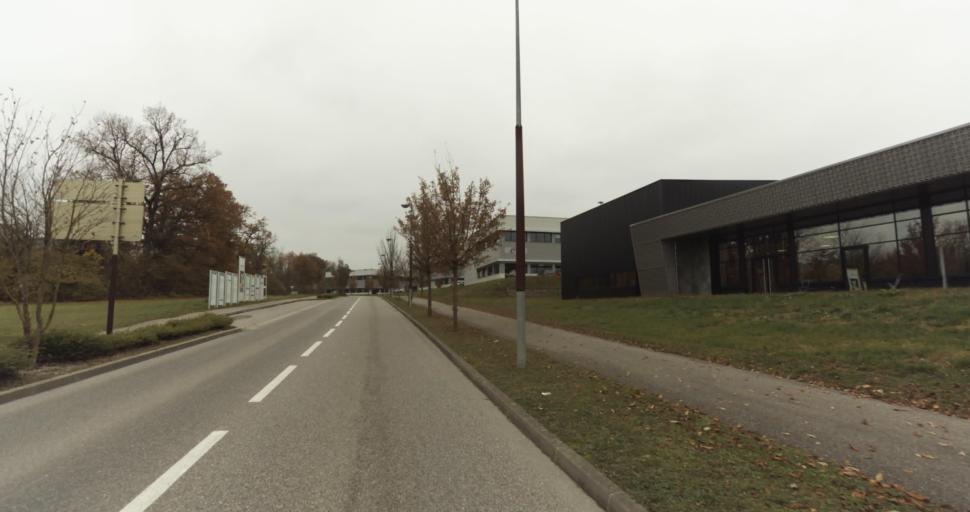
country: FR
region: Rhone-Alpes
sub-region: Departement de la Haute-Savoie
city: Seynod
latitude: 45.8907
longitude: 6.0769
